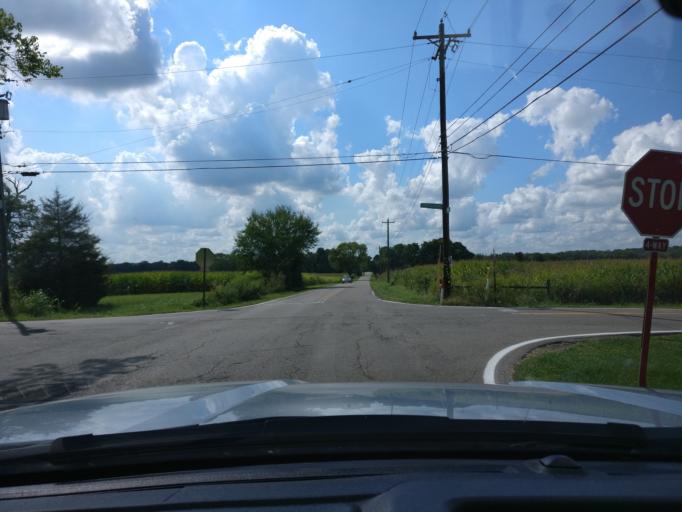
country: US
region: Ohio
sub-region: Warren County
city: Springboro
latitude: 39.5049
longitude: -84.2182
